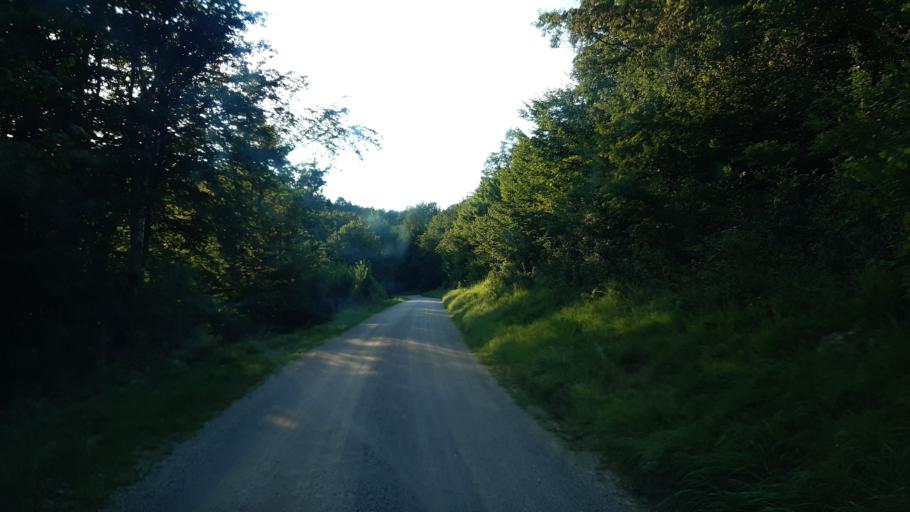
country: SI
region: Kocevje
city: Kocevje
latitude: 45.6672
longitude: 14.9562
